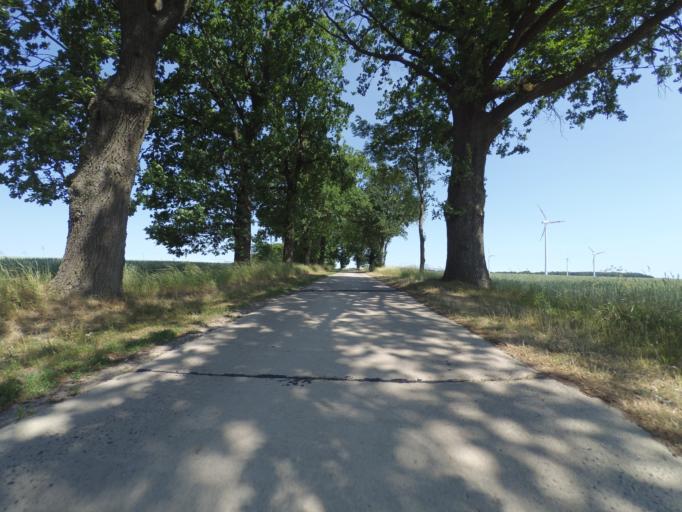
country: DE
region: Brandenburg
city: Gerdshagen
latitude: 53.2643
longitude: 12.2802
